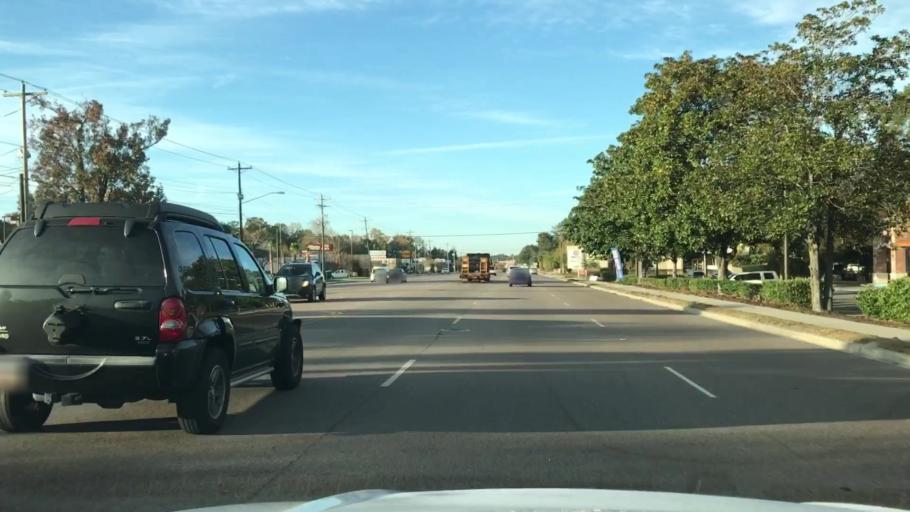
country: US
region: South Carolina
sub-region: Charleston County
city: North Charleston
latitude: 32.8006
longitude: -80.0194
